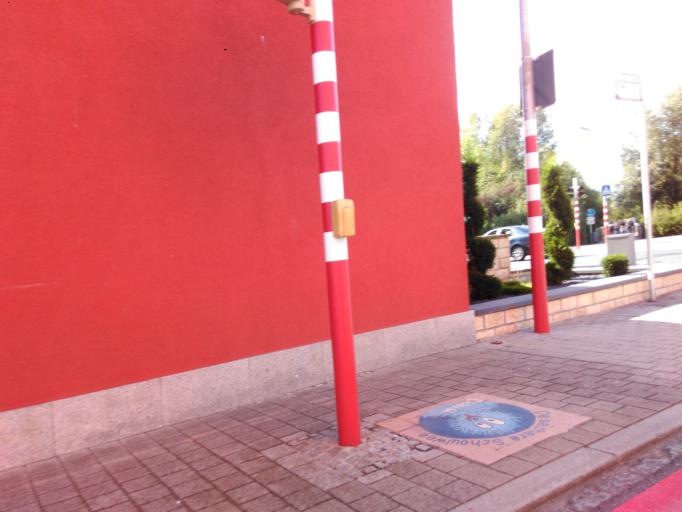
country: LU
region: Luxembourg
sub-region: Canton de Capellen
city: Bascharage
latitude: 49.5642
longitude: 5.9057
